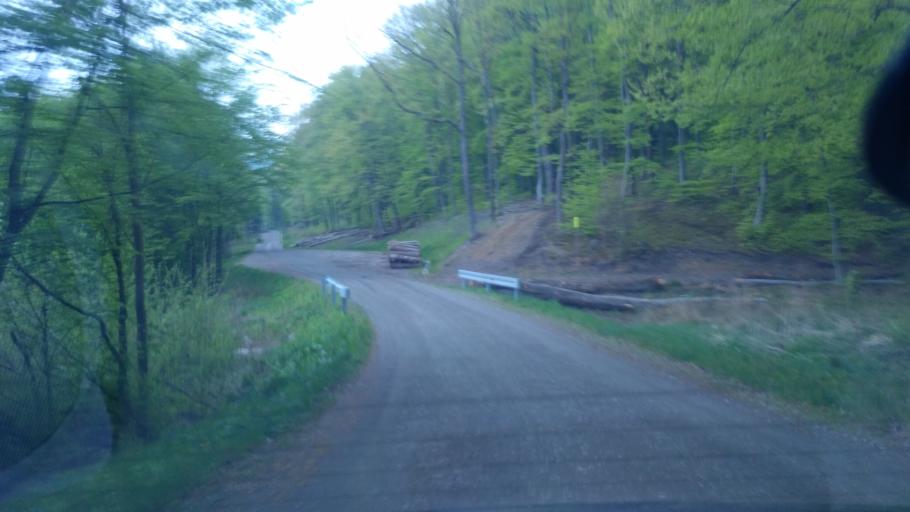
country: PL
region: Subcarpathian Voivodeship
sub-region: Powiat sanocki
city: Sanok
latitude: 49.5667
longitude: 22.2312
